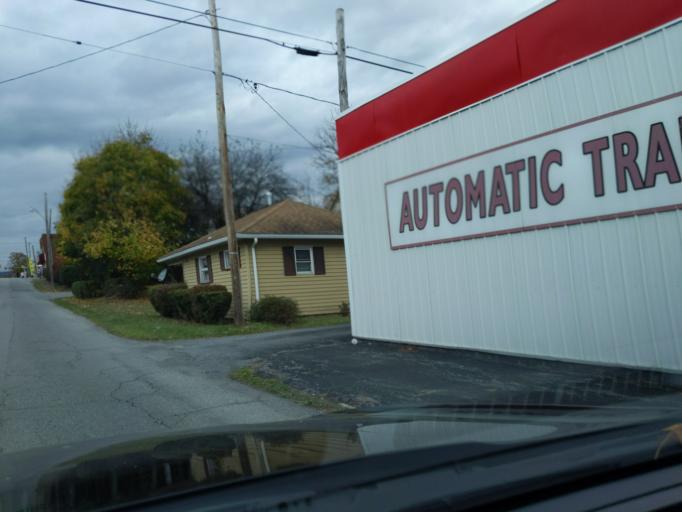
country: US
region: Pennsylvania
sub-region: Blair County
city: Altoona
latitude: 40.5196
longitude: -78.3755
